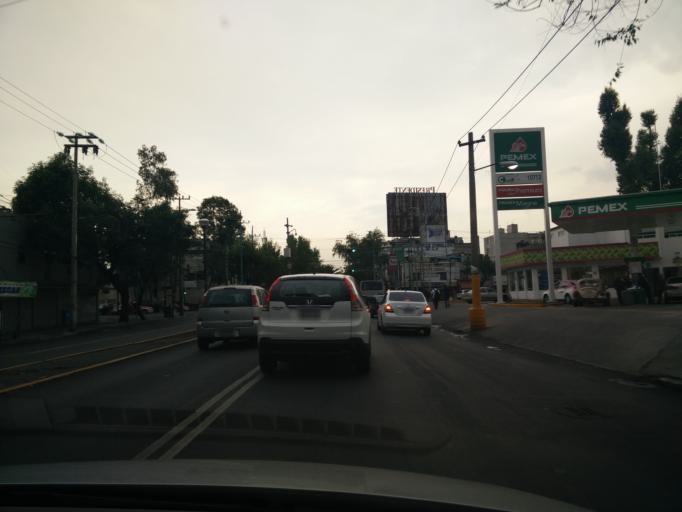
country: MX
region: Mexico City
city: Benito Juarez
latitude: 19.4077
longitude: -99.1496
